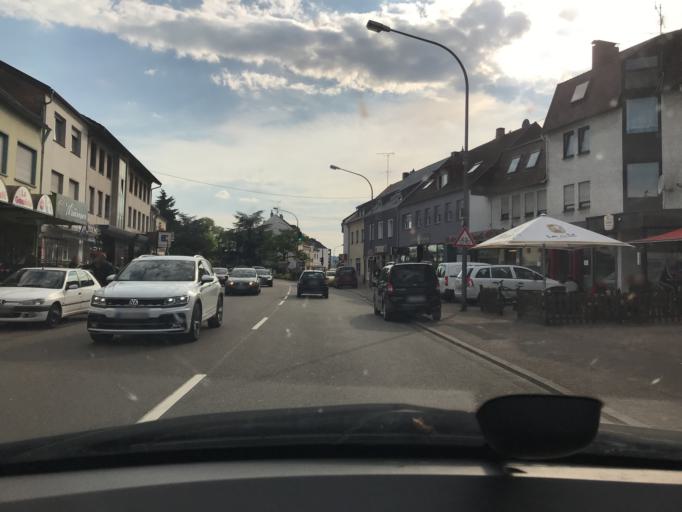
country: DE
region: Saarland
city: Saarlouis
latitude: 49.3267
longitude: 6.7667
